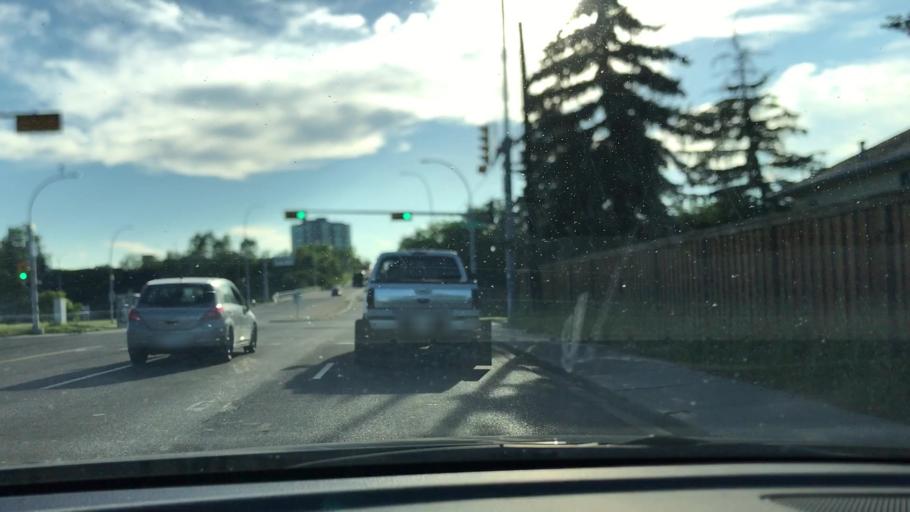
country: CA
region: Alberta
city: Calgary
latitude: 51.0379
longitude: -114.1108
